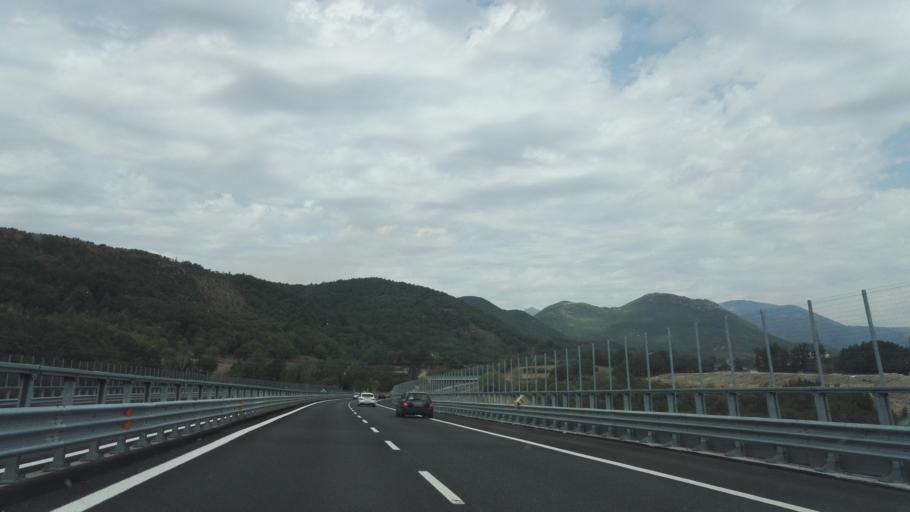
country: IT
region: Calabria
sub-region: Provincia di Cosenza
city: Laino Borgo
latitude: 39.9584
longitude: 15.9344
